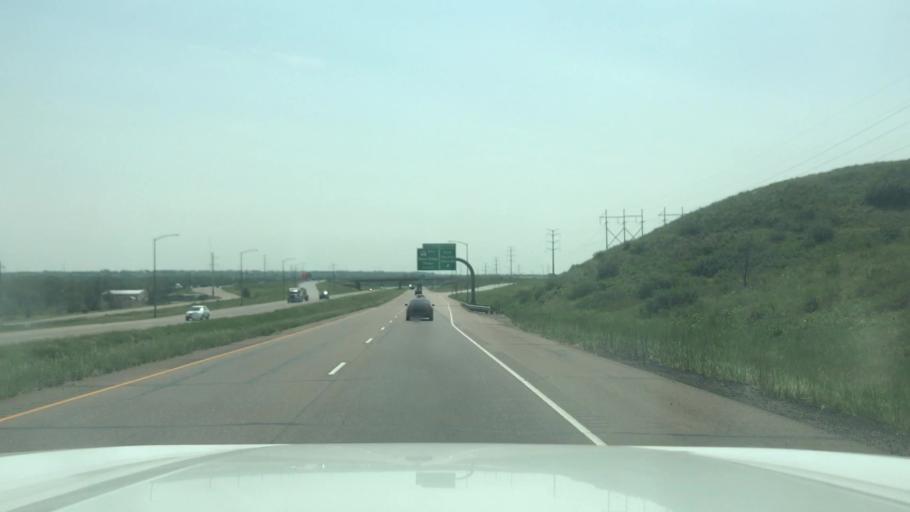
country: US
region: Colorado
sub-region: El Paso County
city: Security-Widefield
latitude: 38.7296
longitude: -104.7382
